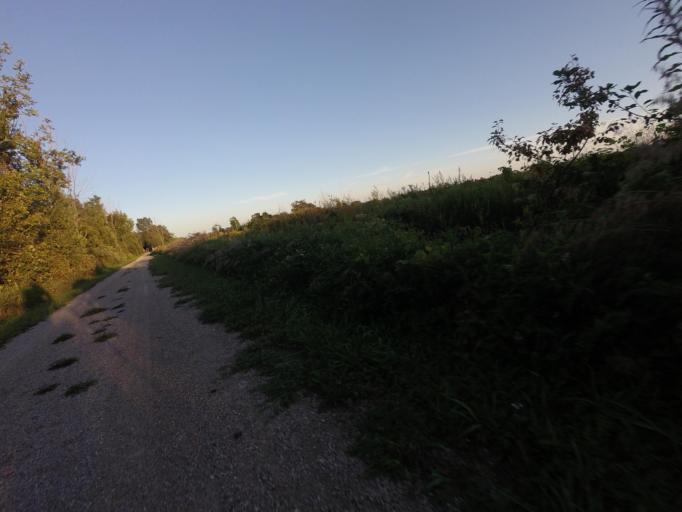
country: CA
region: Ontario
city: Goderich
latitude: 43.7573
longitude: -81.6829
